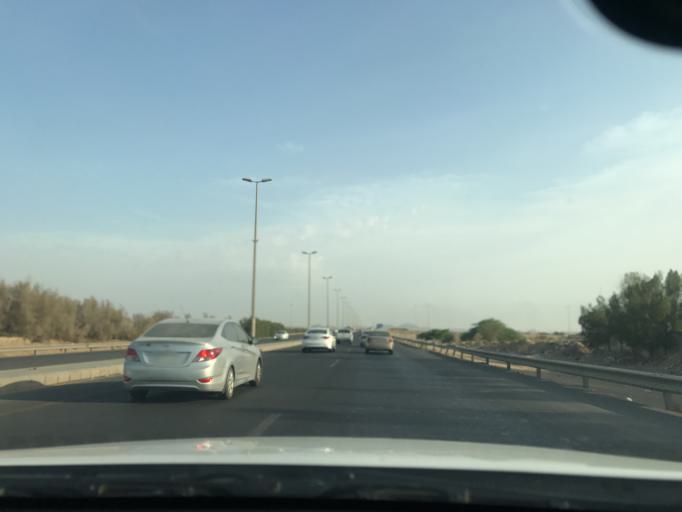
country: SA
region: Makkah
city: Jeddah
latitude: 21.3950
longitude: 39.4268
